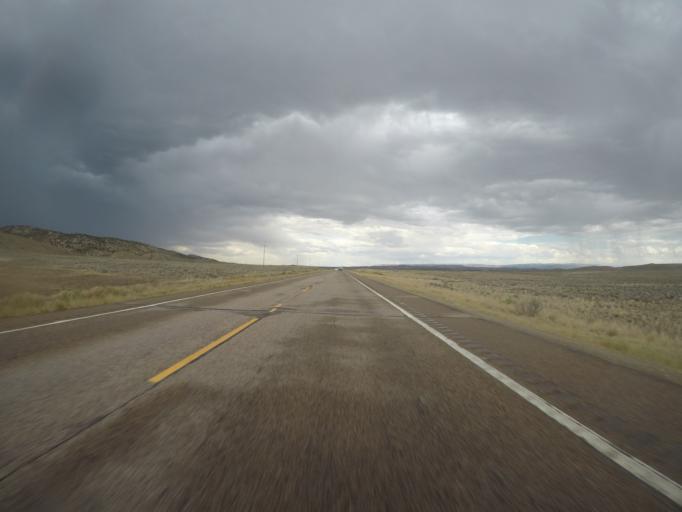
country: US
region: Colorado
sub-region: Rio Blanco County
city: Rangely
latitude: 40.2401
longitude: -108.9270
